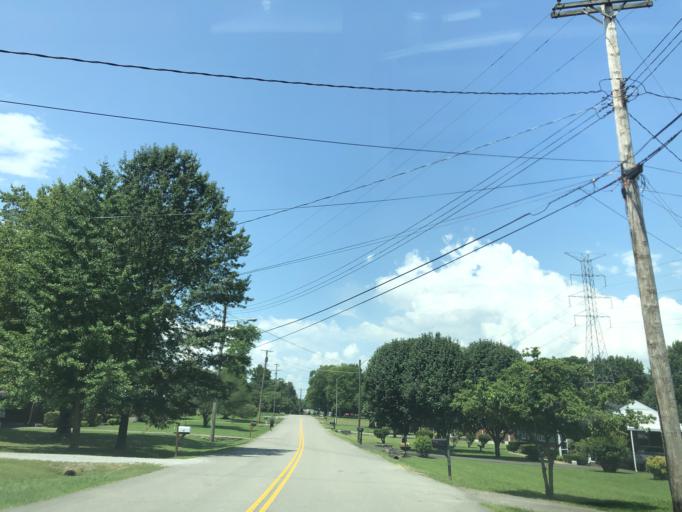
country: US
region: Tennessee
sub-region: Davidson County
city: Lakewood
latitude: 36.1563
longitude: -86.6604
